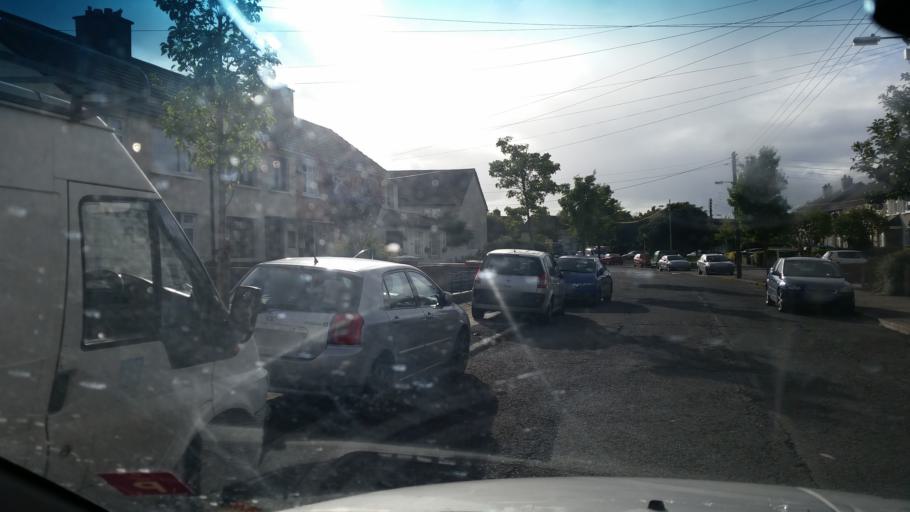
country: IE
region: Leinster
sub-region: Dublin City
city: Finglas
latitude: 53.3827
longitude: -6.2817
